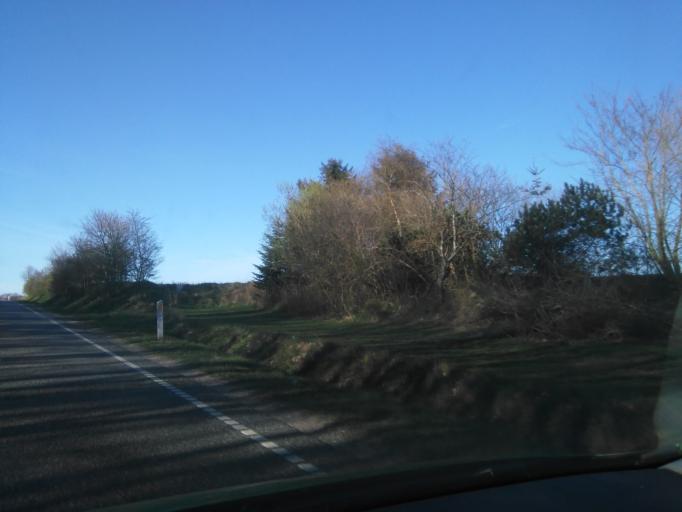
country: DK
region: Central Jutland
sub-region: Ringkobing-Skjern Kommune
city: Videbaek
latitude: 56.0787
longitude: 8.5072
